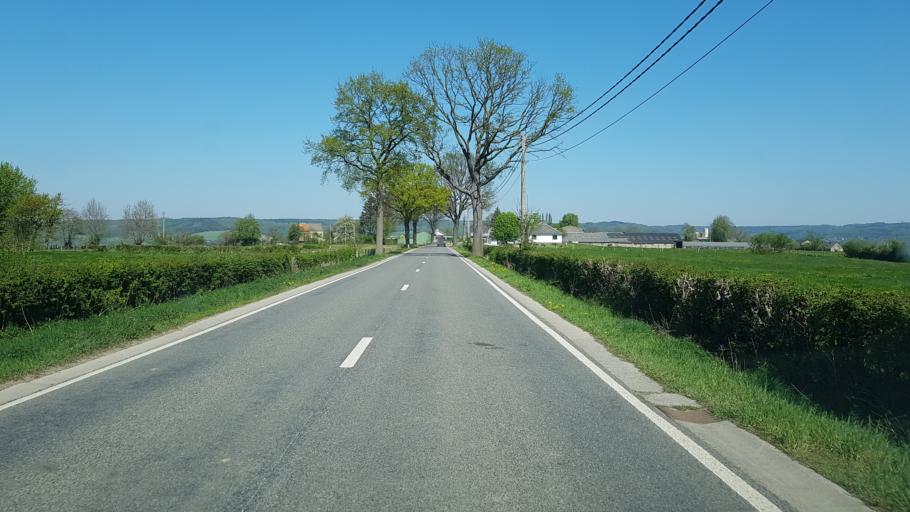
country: BE
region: Wallonia
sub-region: Province de Liege
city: Plombieres
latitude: 50.7307
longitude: 5.9358
